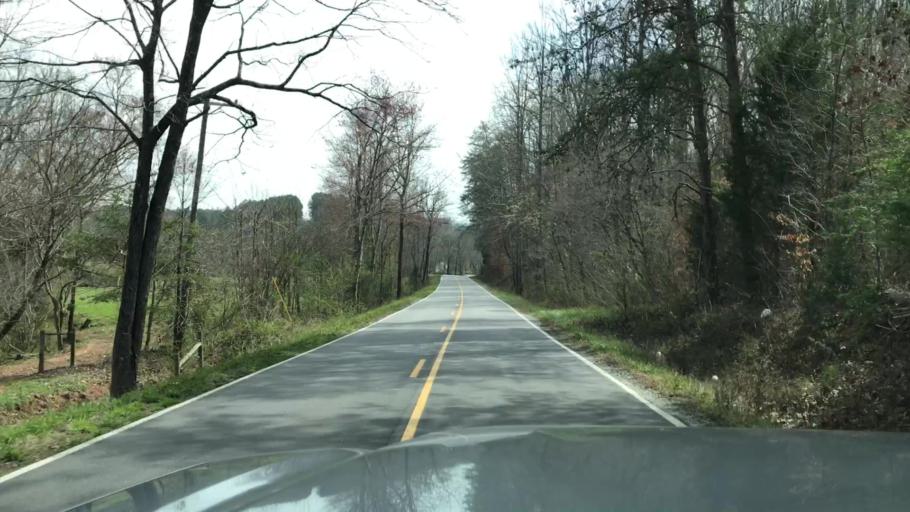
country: US
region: North Carolina
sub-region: Rutherford County
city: Spindale
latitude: 35.4507
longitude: -81.8819
